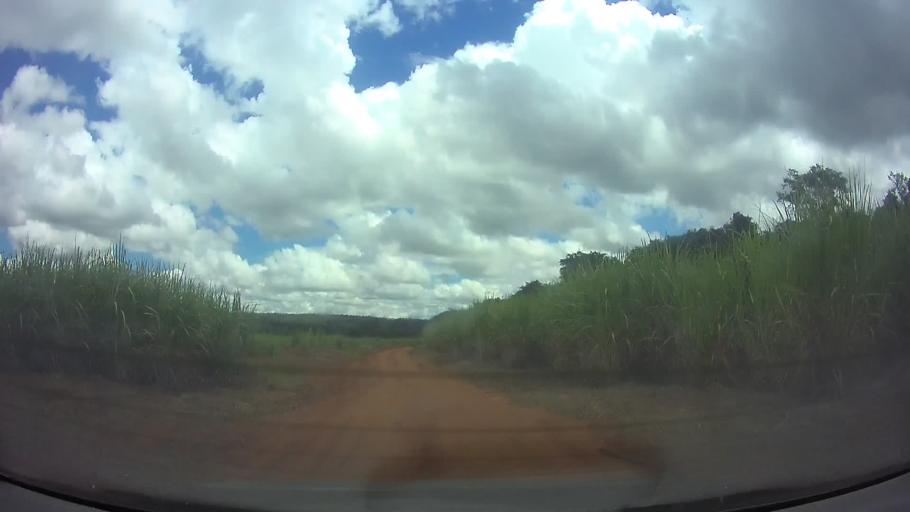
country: PY
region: Paraguari
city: La Colmena
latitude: -25.9509
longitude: -56.7797
